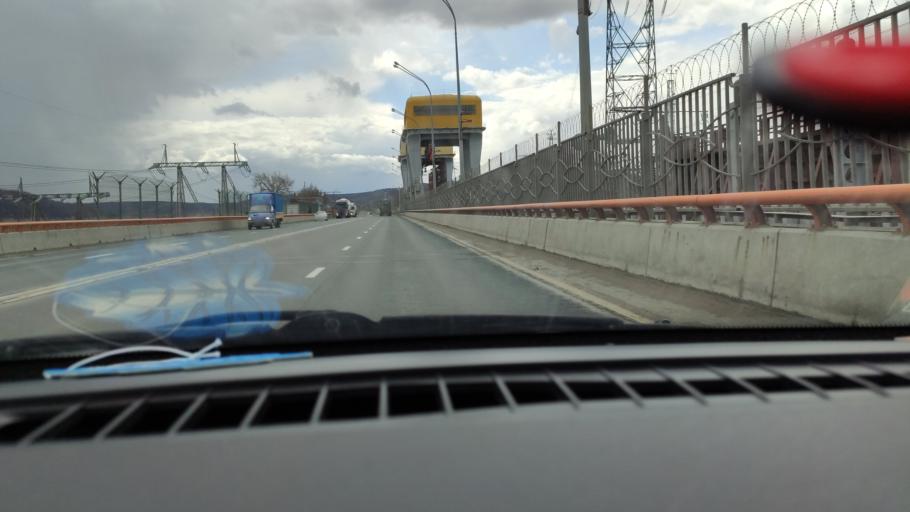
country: RU
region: Samara
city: Zhigulevsk
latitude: 53.4501
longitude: 49.4900
